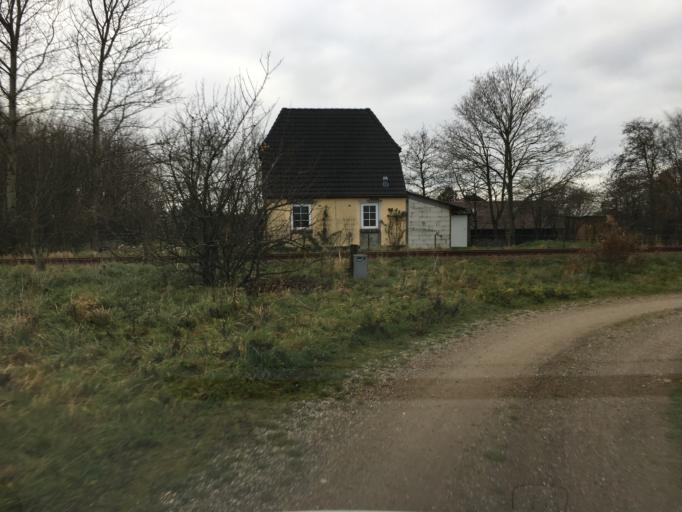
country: DK
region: South Denmark
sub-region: Tonder Kommune
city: Tonder
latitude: 54.9478
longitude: 8.8579
